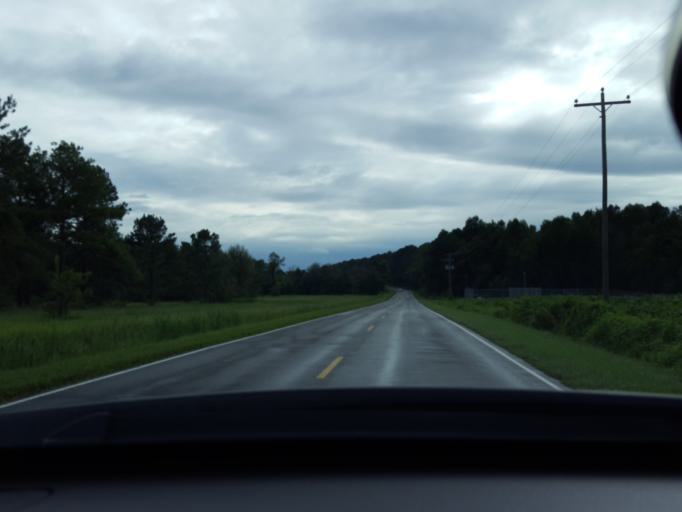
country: US
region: North Carolina
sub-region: Duplin County
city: Rose Hill
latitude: 34.9130
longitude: -78.0322
